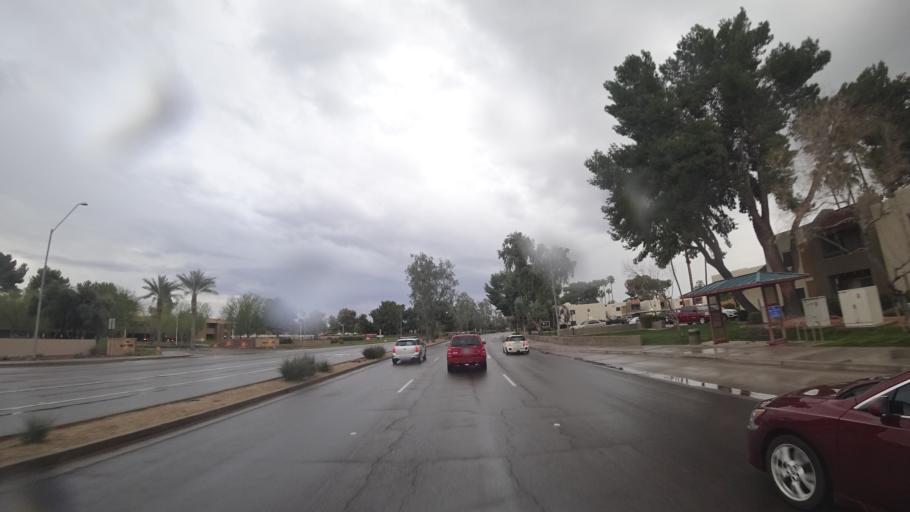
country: US
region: Arizona
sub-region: Maricopa County
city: Scottsdale
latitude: 33.5541
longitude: -111.8988
